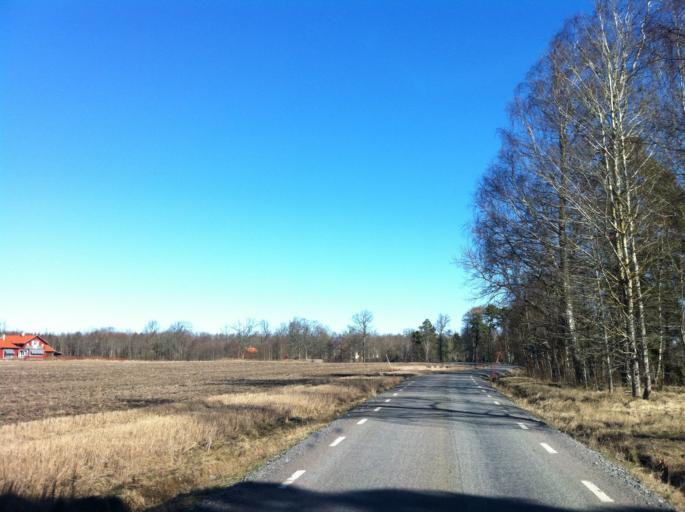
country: SE
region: Vaestra Goetaland
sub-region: Grastorps Kommun
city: Graestorp
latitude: 58.4073
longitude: 12.5855
